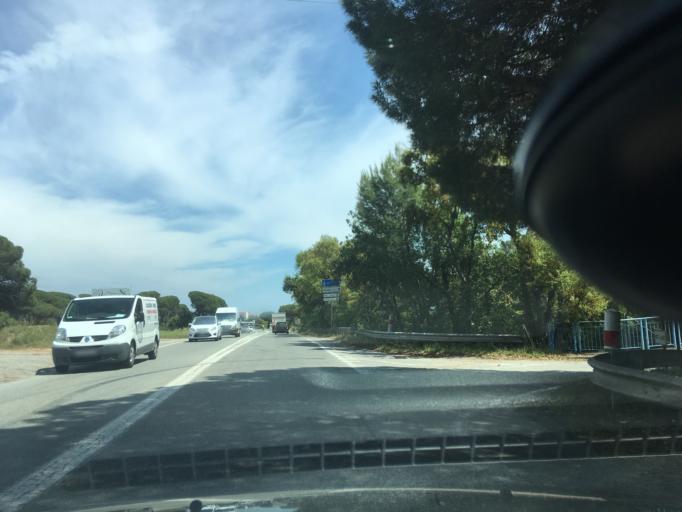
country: FR
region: Provence-Alpes-Cote d'Azur
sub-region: Departement du Var
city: Puget-sur-Argens
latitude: 43.4595
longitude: 6.6665
